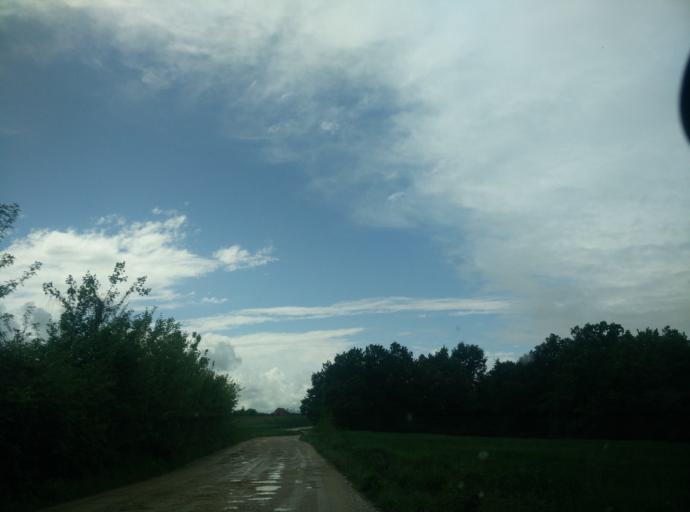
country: BA
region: Brcko
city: Brcko
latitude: 44.7835
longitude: 18.8215
